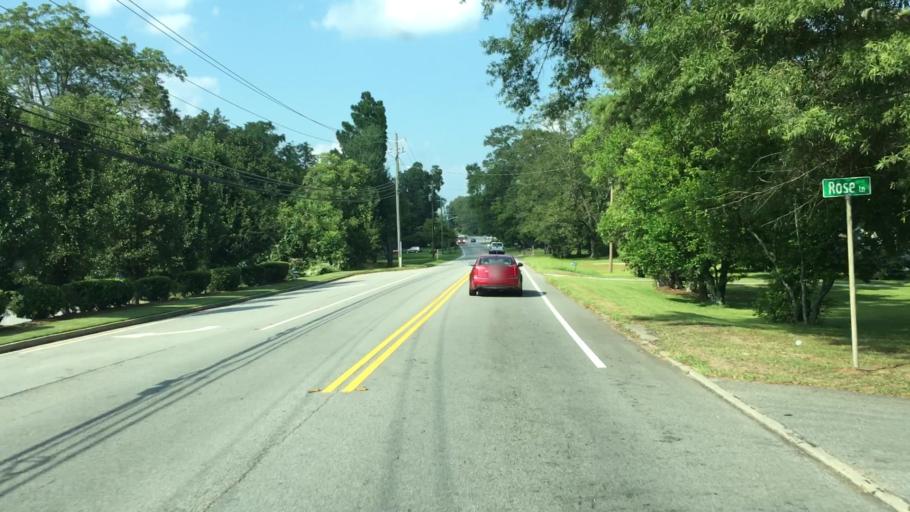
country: US
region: Georgia
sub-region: Walton County
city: Social Circle
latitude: 33.6663
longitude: -83.7122
